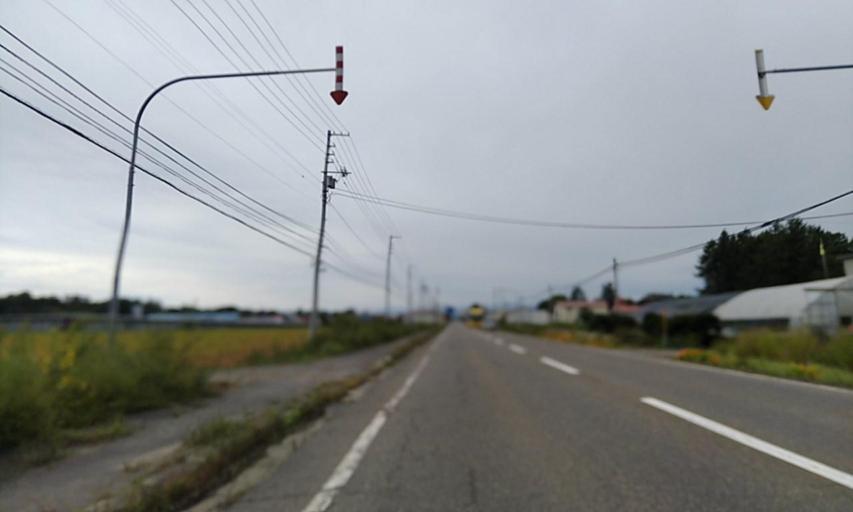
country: JP
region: Hokkaido
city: Obihiro
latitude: 42.7980
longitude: 143.1681
